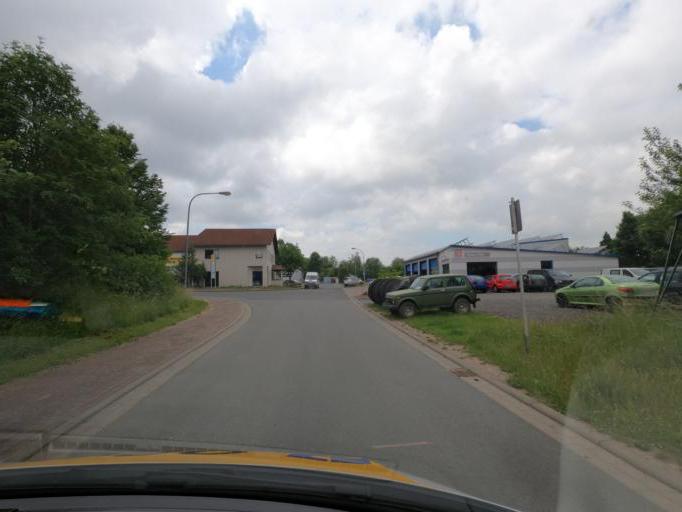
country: DE
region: Thuringia
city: Heilbad Heiligenstadt
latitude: 51.3871
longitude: 10.1684
